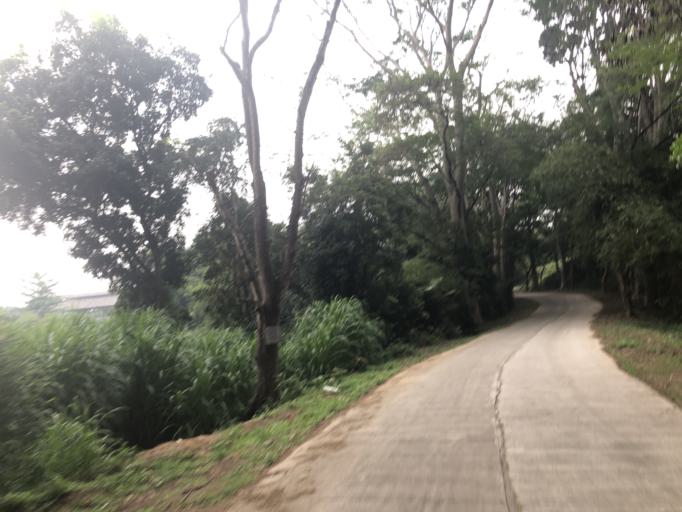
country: ID
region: West Java
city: Ciampea
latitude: -6.5555
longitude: 106.7177
